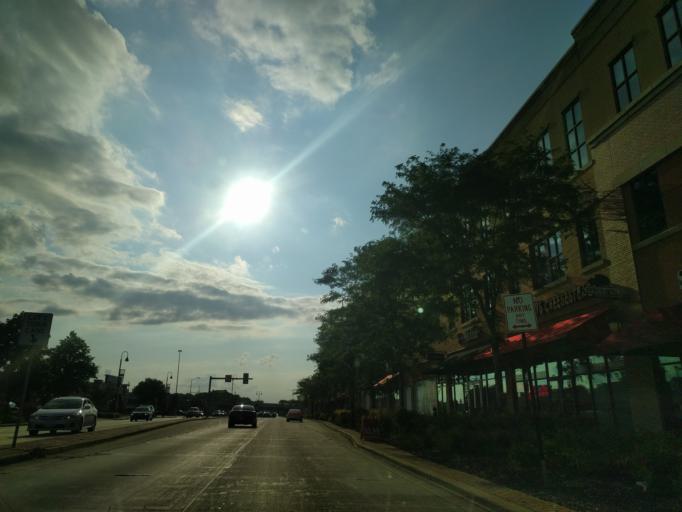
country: US
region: Wisconsin
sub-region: Milwaukee County
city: Whitefish Bay
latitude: 43.1187
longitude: -87.9143
